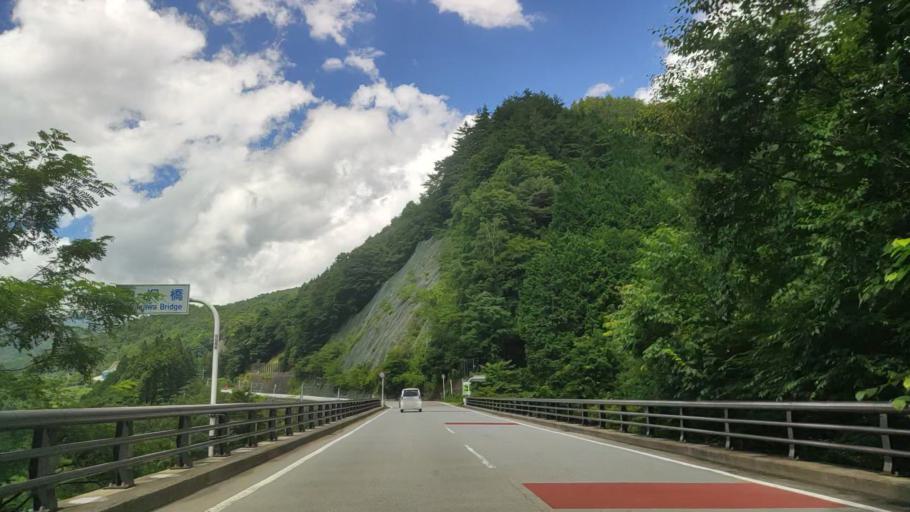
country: JP
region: Yamanashi
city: Enzan
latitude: 35.8244
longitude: 138.7626
